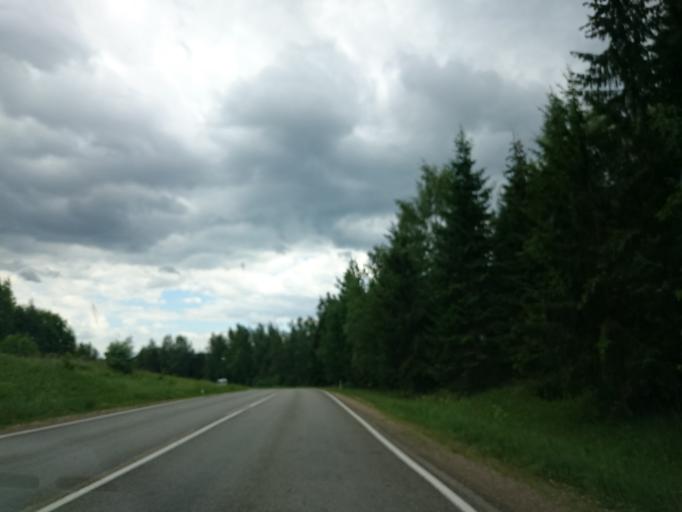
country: LV
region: Ludzas Rajons
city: Ludza
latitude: 56.5356
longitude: 27.5808
